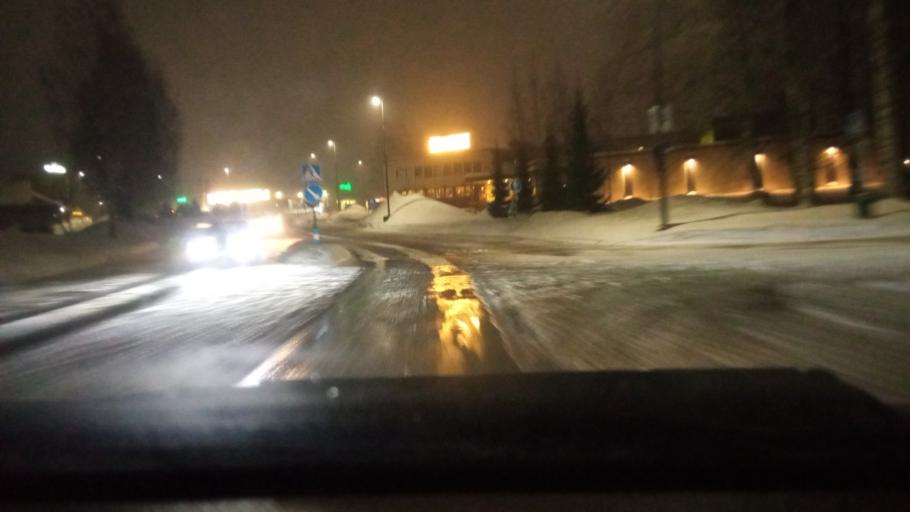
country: FI
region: Southern Ostrobothnia
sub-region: Jaerviseutu
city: Alajaervi
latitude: 63.0022
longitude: 23.8123
